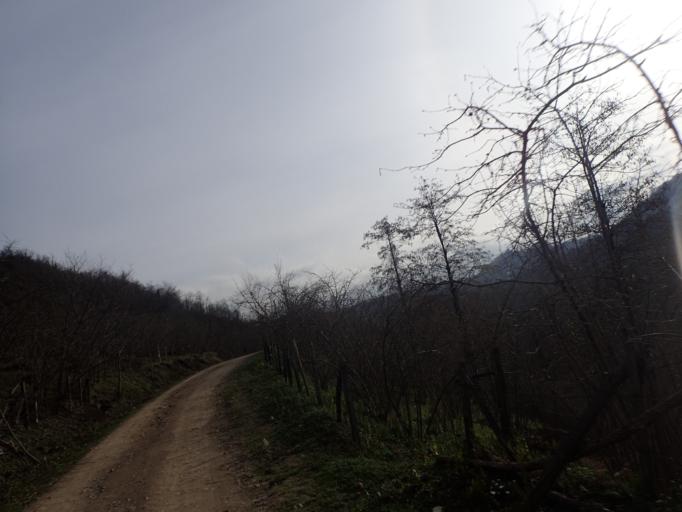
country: TR
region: Ordu
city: Camas
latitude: 40.9343
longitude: 37.5134
